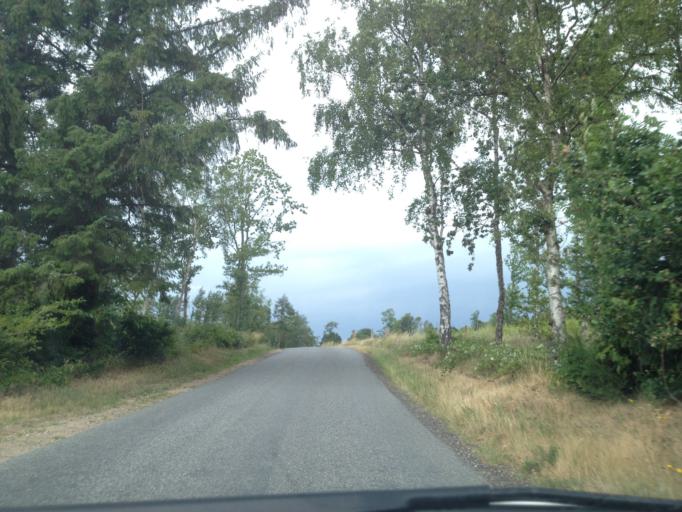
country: DK
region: Central Jutland
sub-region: Syddjurs Kommune
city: Ebeltoft
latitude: 56.1658
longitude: 10.6801
